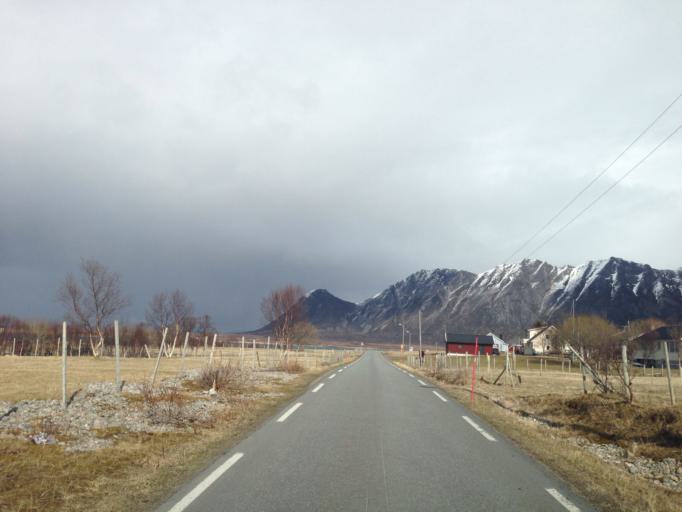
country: NO
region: Nordland
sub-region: Vagan
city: Svolvaer
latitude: 68.4024
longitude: 14.5087
